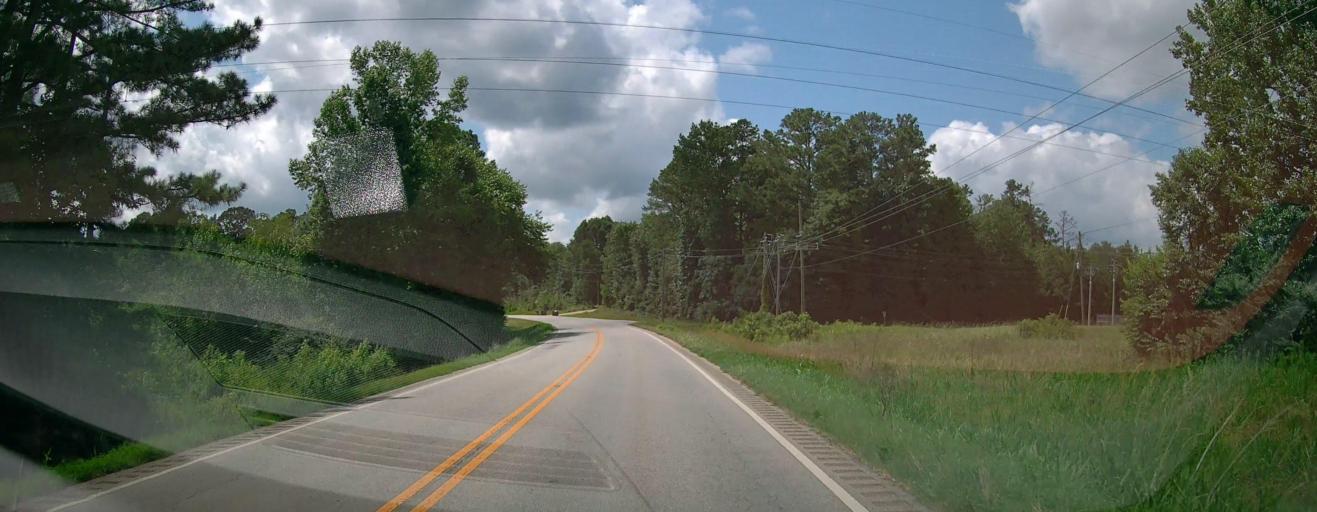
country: US
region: Georgia
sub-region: Carroll County
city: Bowdon
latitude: 33.5342
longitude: -85.3672
